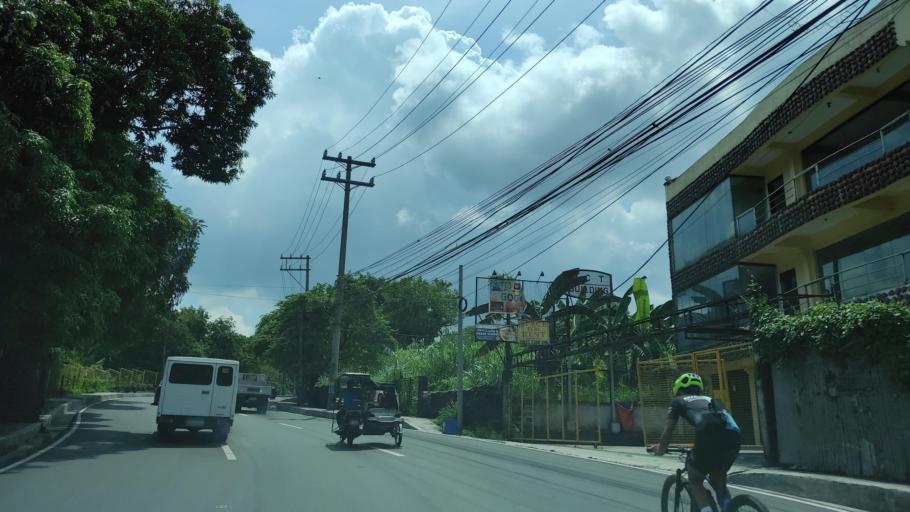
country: PH
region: Calabarzon
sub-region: Province of Rizal
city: Taytay
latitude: 14.5863
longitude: 121.1643
